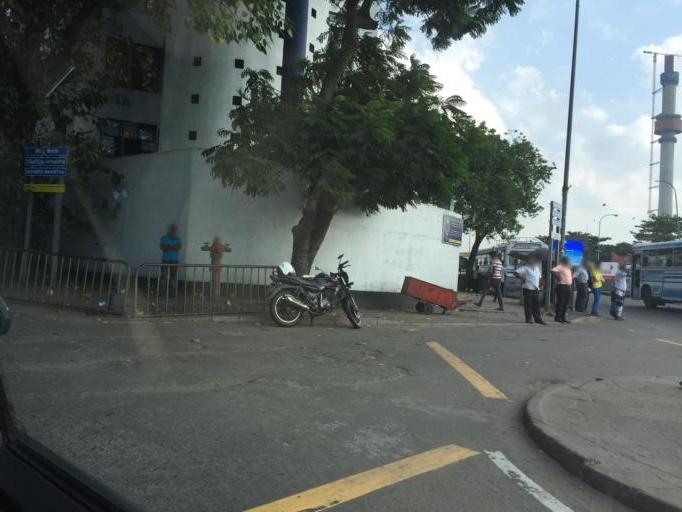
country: LK
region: Western
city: Colombo
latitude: 6.9343
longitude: 79.8559
